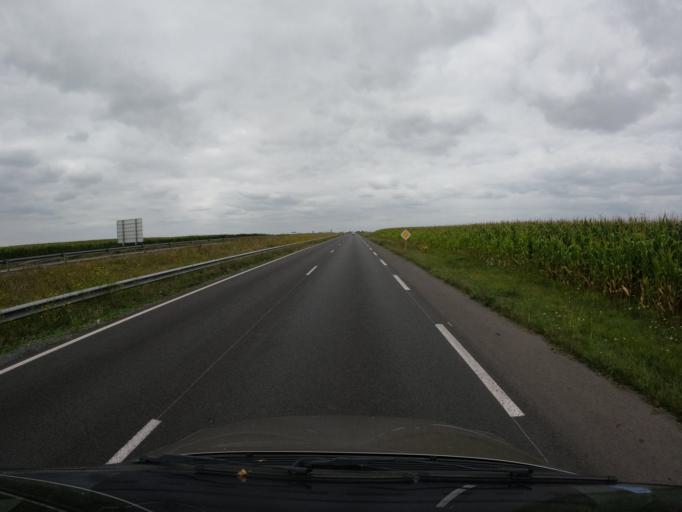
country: FR
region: Pays de la Loire
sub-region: Departement de la Vendee
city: Maillezais
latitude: 46.4230
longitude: -0.7131
